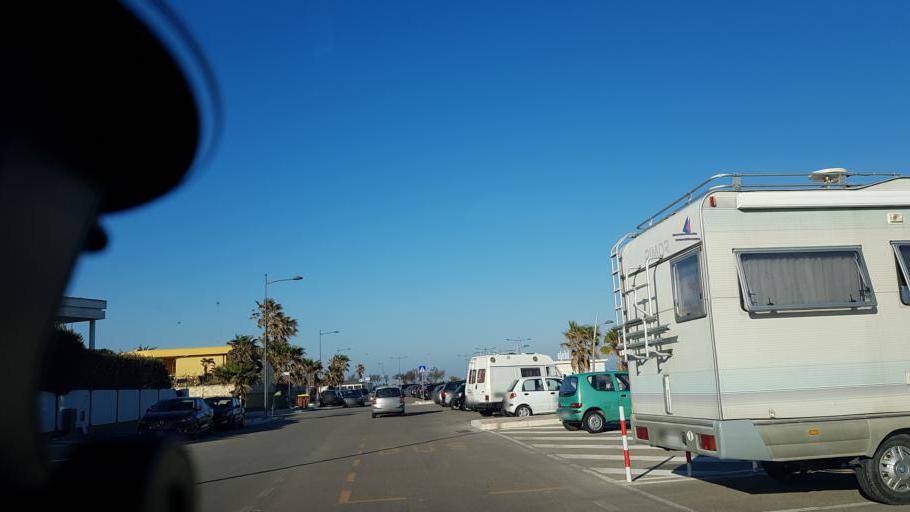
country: IT
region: Apulia
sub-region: Provincia di Lecce
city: Struda
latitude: 40.3880
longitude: 18.3044
